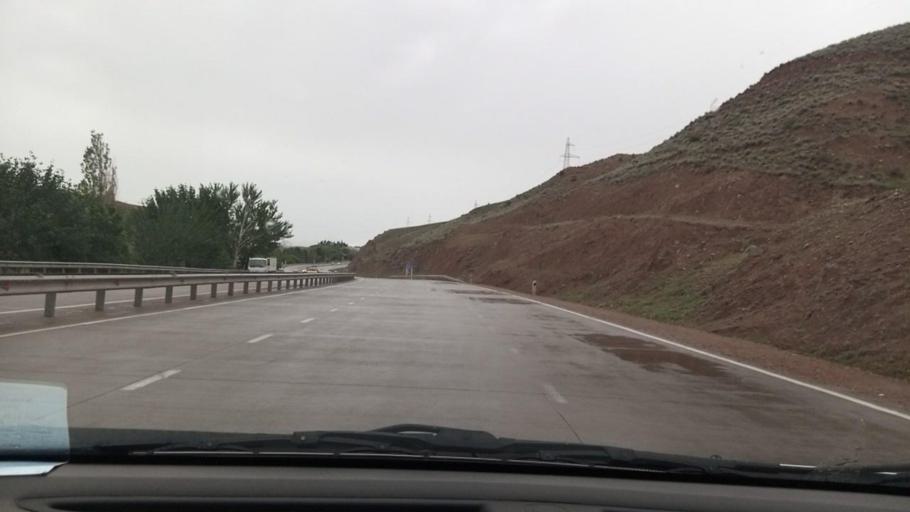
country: TJ
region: Viloyati Sughd
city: Shaydon
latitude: 40.9522
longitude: 70.6760
